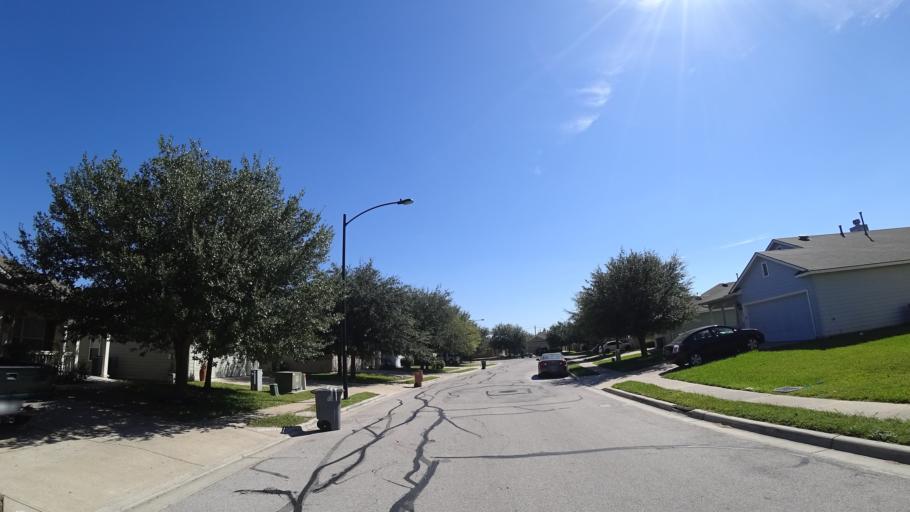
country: US
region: Texas
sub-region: Travis County
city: Austin
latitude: 30.1975
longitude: -97.6943
